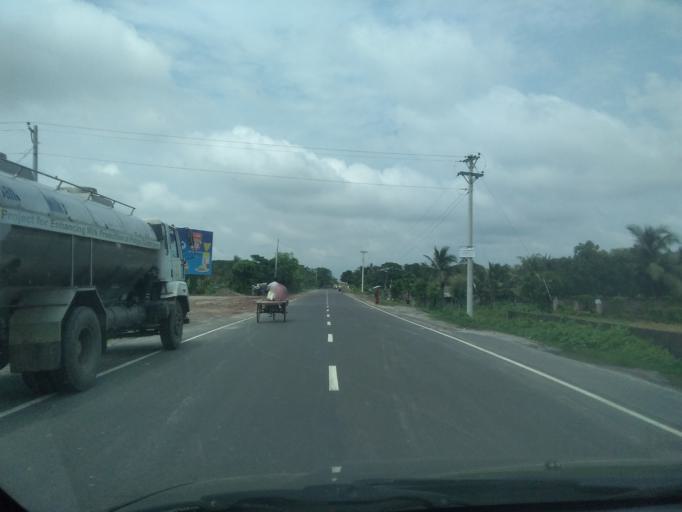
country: BD
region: Khulna
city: Kesabpur
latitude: 22.7910
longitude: 89.2200
